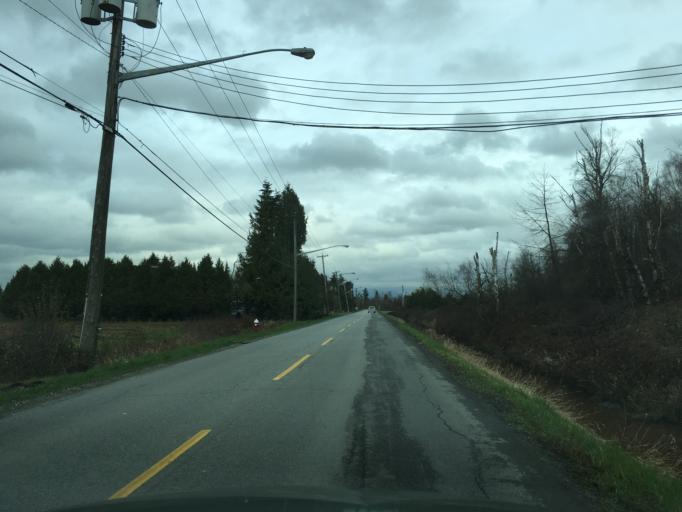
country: CA
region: British Columbia
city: Richmond
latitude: 49.1576
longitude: -123.0689
